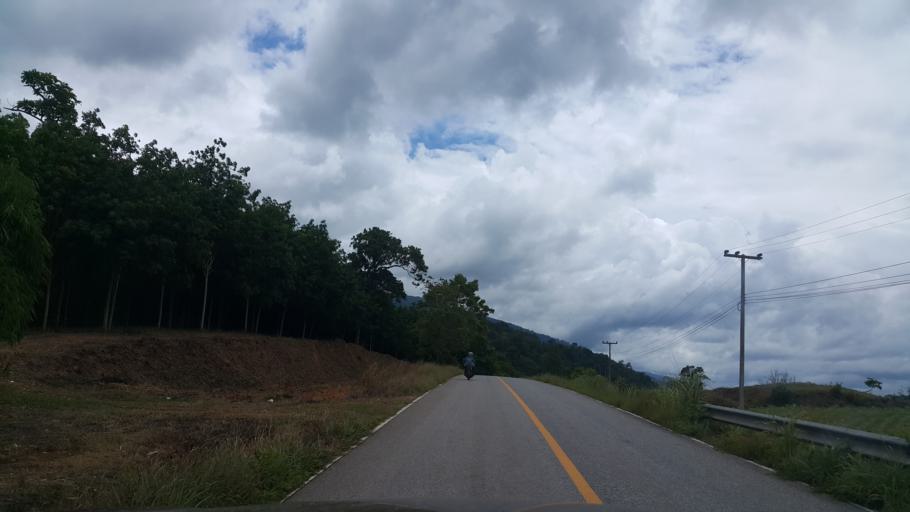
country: TH
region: Phitsanulok
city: Chat Trakan
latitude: 17.3974
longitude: 100.7617
